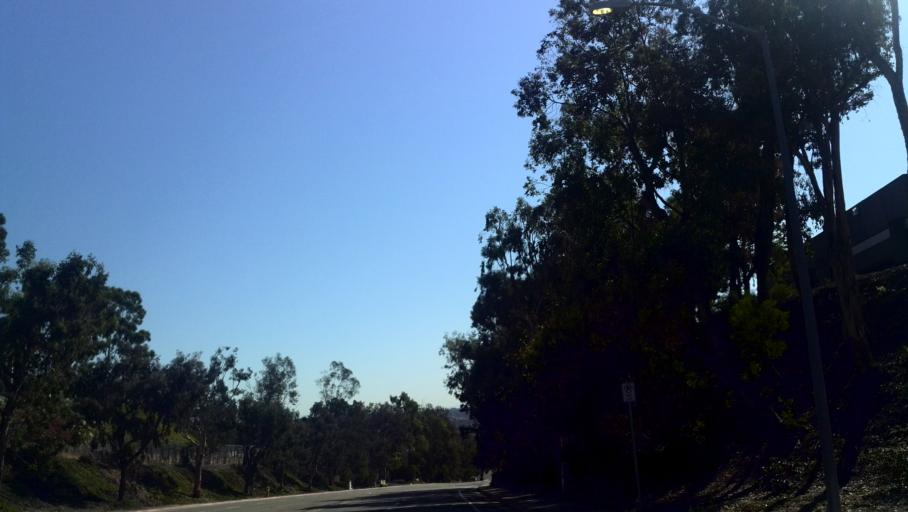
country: US
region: California
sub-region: San Diego County
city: San Diego
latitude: 32.8123
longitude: -117.1203
